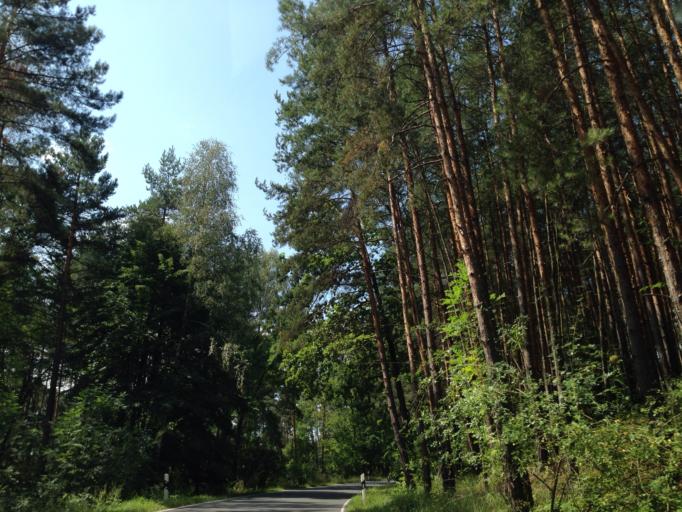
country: DE
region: Thuringia
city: Herschdorf
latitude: 50.7093
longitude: 11.5533
